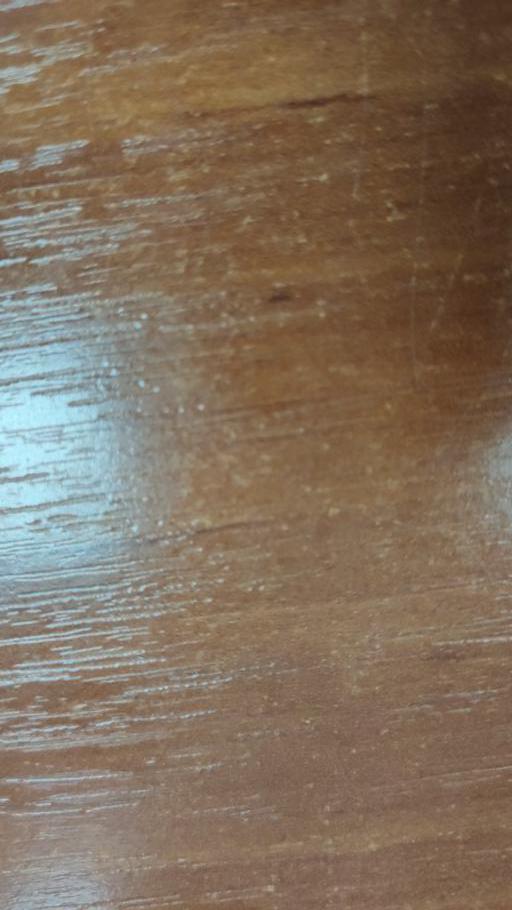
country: RU
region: Moskovskaya
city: Solnechnogorsk
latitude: 56.1872
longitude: 37.0214
